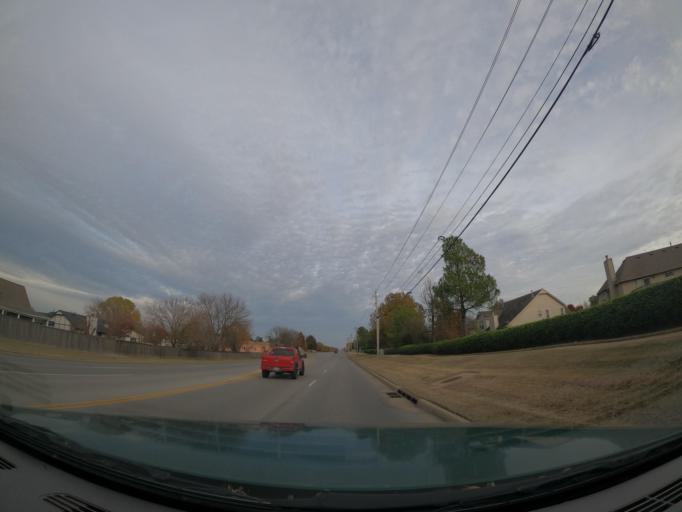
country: US
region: Oklahoma
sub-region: Tulsa County
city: Broken Arrow
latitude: 36.0608
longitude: -95.8442
